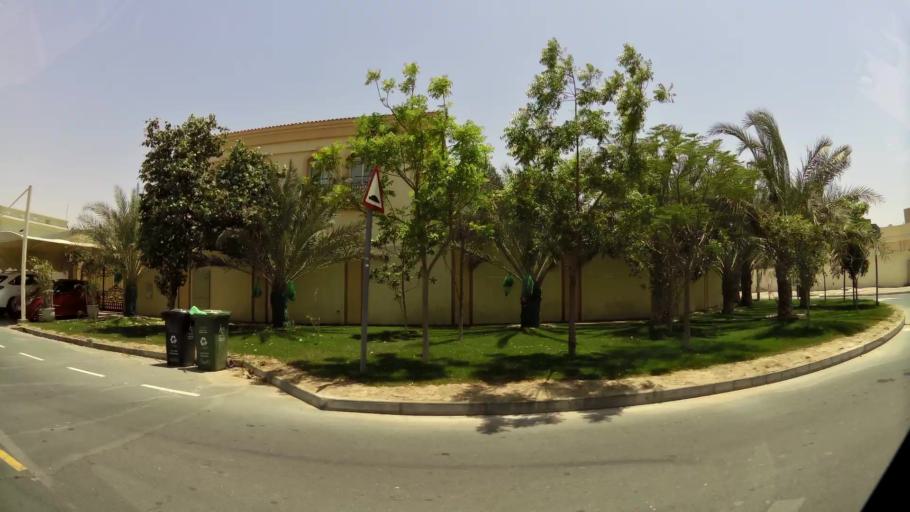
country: AE
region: Dubai
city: Dubai
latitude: 25.0847
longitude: 55.2081
